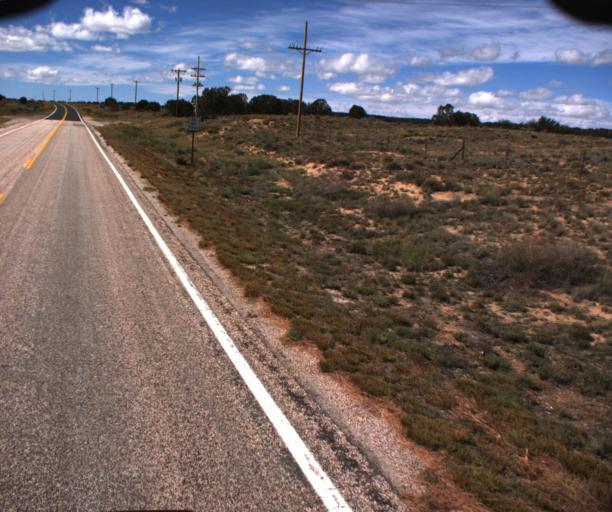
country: US
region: New Mexico
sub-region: McKinley County
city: Zuni Pueblo
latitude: 35.0204
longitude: -109.0448
